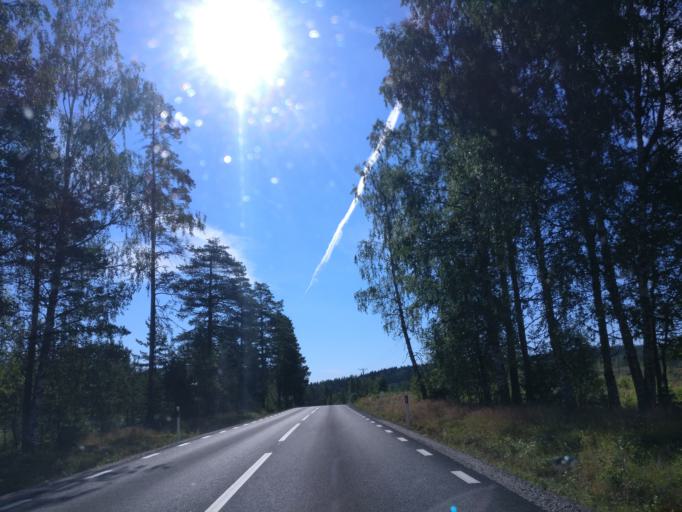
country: SE
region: Vaermland
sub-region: Hagfors Kommun
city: Hagfors
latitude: 60.0482
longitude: 13.7975
